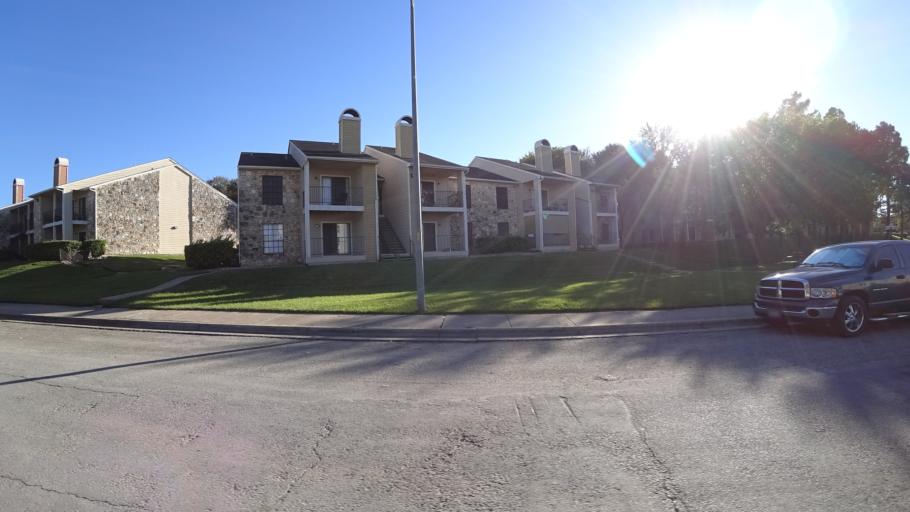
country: US
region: Texas
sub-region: Travis County
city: Austin
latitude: 30.2301
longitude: -97.7199
